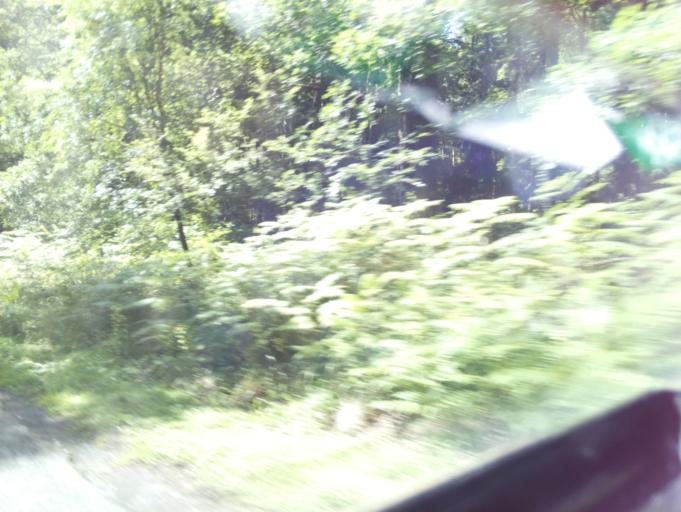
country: GB
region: England
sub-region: Gloucestershire
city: Cinderford
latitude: 51.7760
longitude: -2.5072
